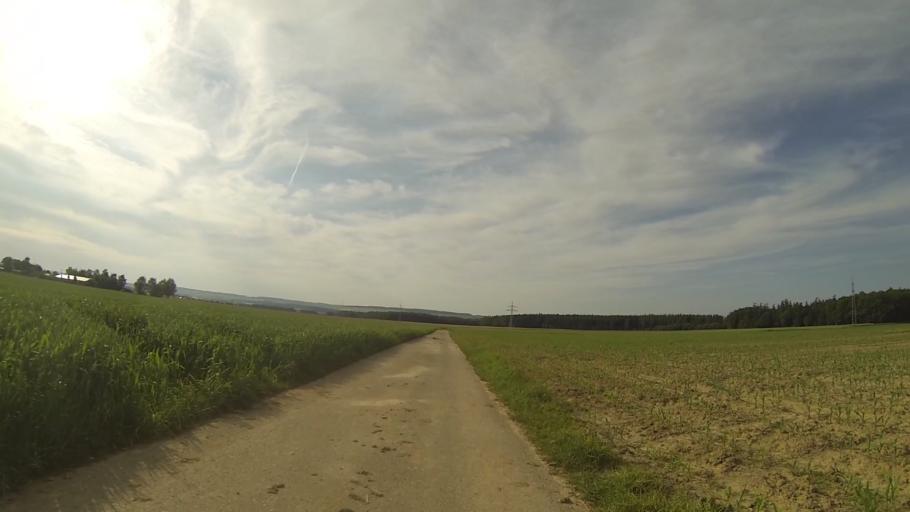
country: DE
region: Baden-Wuerttemberg
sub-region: Tuebingen Region
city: Staig
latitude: 48.3374
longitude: 9.9646
